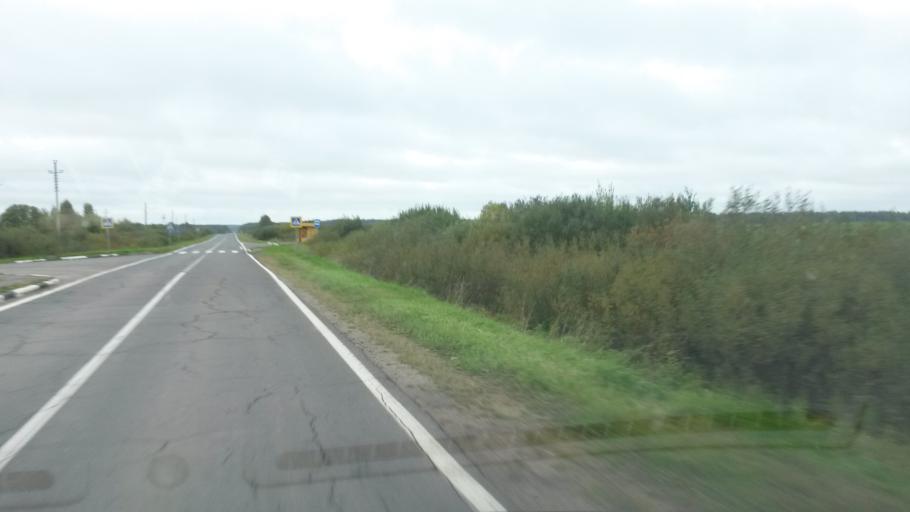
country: RU
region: Jaroslavl
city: Tutayev
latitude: 57.9502
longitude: 39.4459
